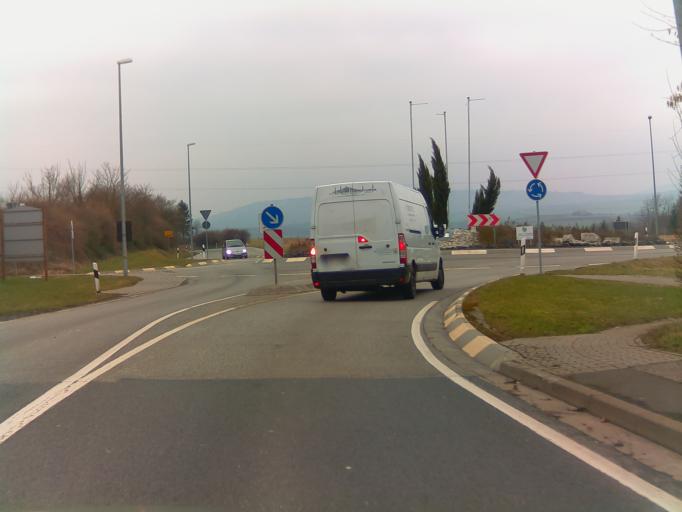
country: DE
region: Rheinland-Pfalz
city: Sulzheim
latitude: 49.8395
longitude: 8.1065
